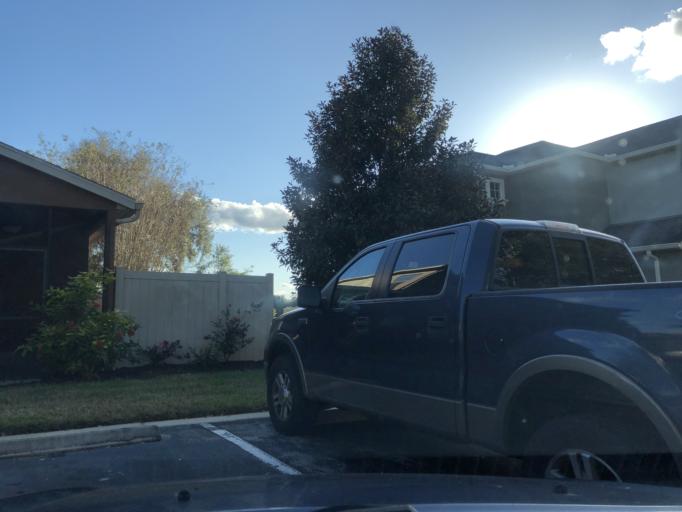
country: US
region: Florida
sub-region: Seminole County
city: Goldenrod
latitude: 28.6165
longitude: -81.2641
